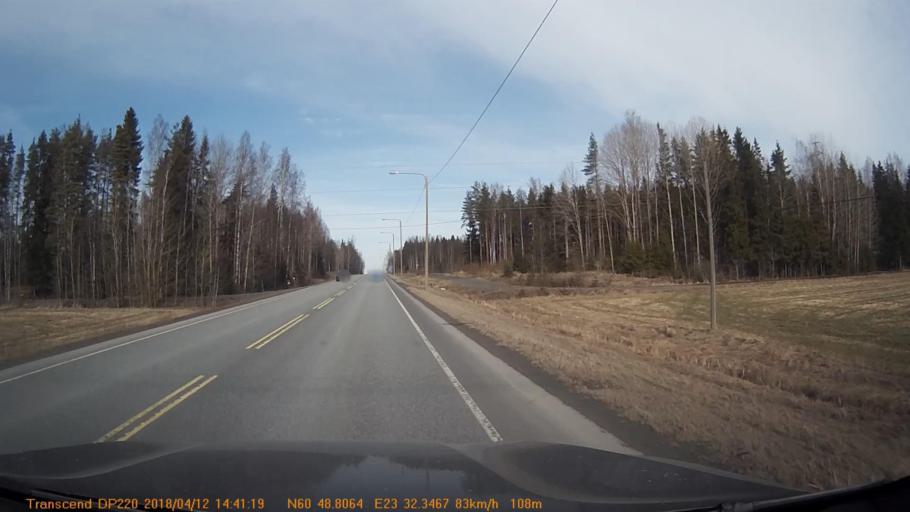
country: FI
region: Haeme
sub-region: Forssa
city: Jokioinen
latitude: 60.8137
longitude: 23.5396
